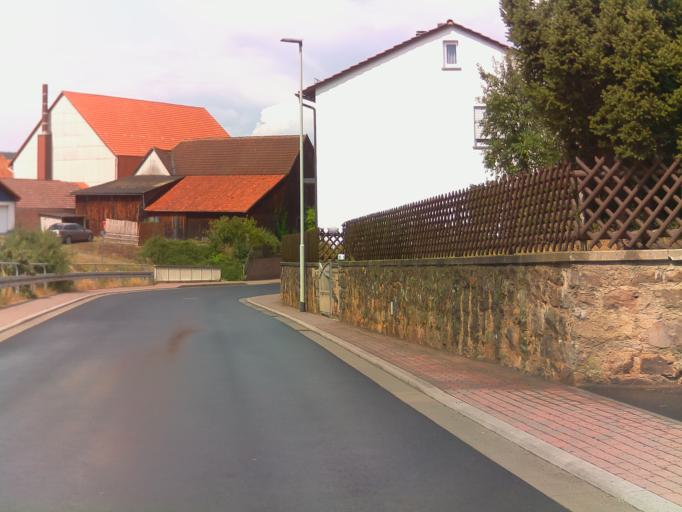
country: DE
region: Hesse
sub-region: Regierungsbezirk Giessen
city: Lauterbach
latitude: 50.6235
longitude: 9.4405
